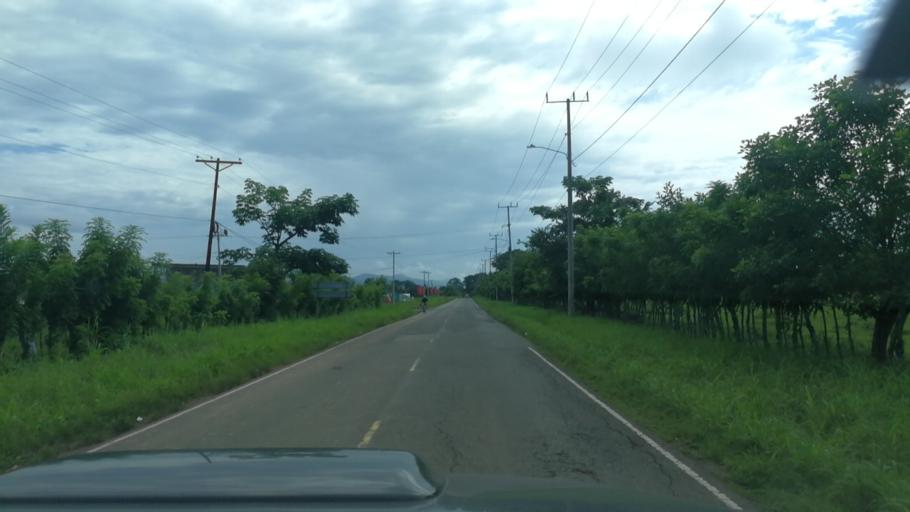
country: PA
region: Panama
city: Paso Blanco
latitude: 9.1088
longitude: -79.2677
